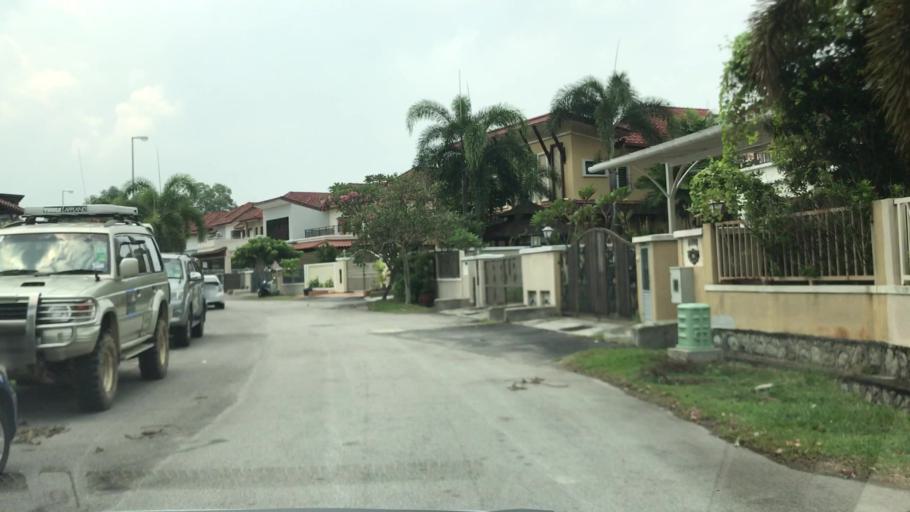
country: MY
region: Putrajaya
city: Putrajaya
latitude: 2.9877
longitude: 101.6674
